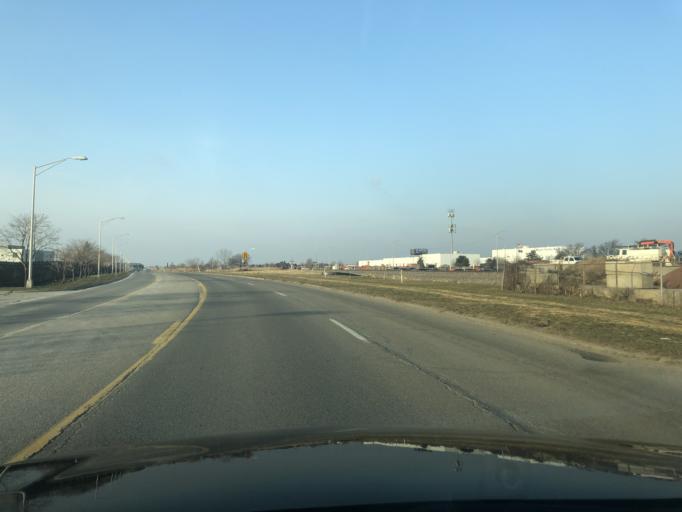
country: US
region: Michigan
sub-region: Wayne County
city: Inkster
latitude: 42.2389
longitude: -83.3305
